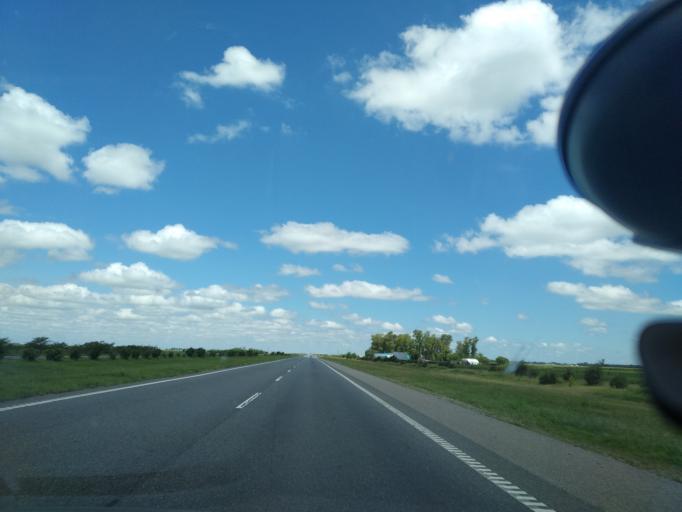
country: AR
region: Cordoba
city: Oliva
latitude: -31.9922
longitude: -63.5613
